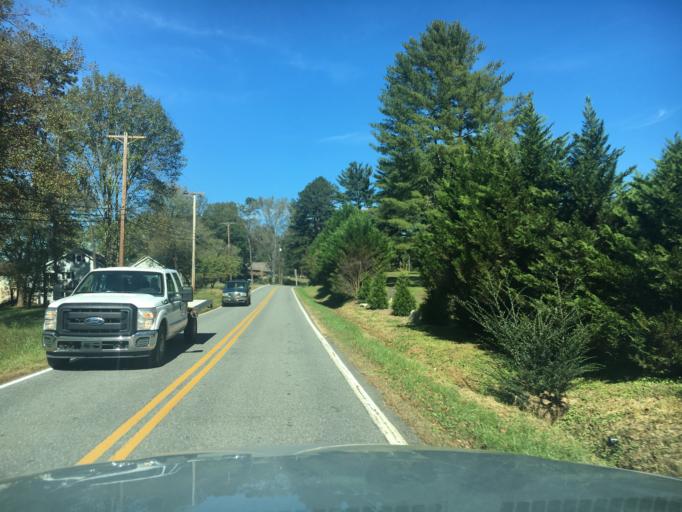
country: US
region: North Carolina
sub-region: Burke County
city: Salem
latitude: 35.7228
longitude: -81.7156
